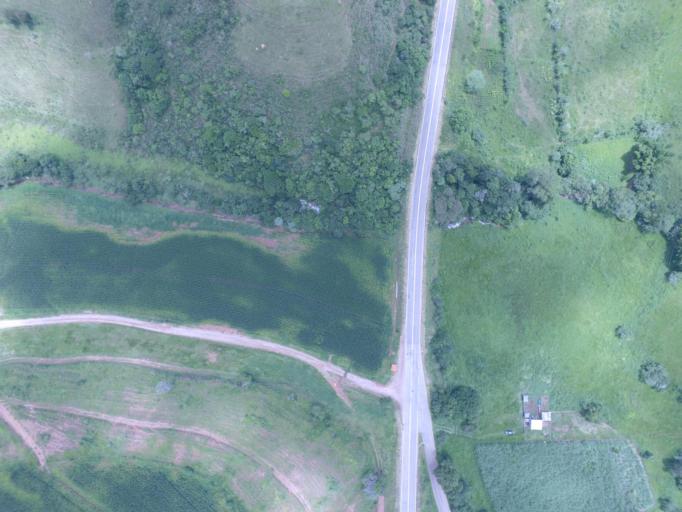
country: BR
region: Minas Gerais
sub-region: Tiradentes
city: Tiradentes
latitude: -21.0829
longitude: -44.0751
